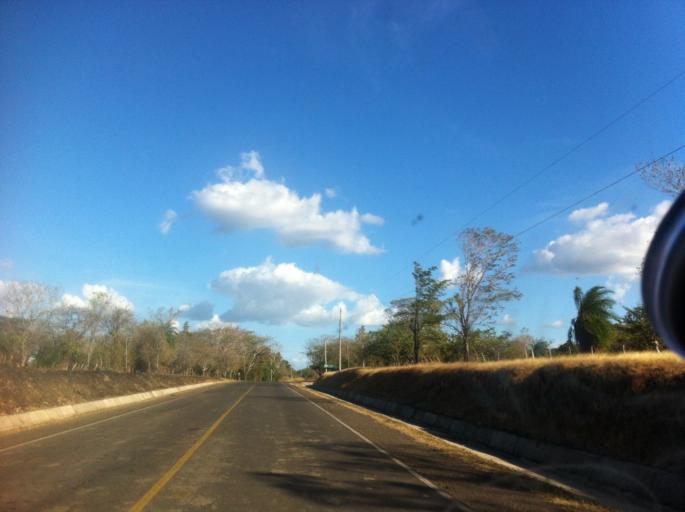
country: NI
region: Chontales
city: Acoyapa
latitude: 11.8926
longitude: -85.1126
